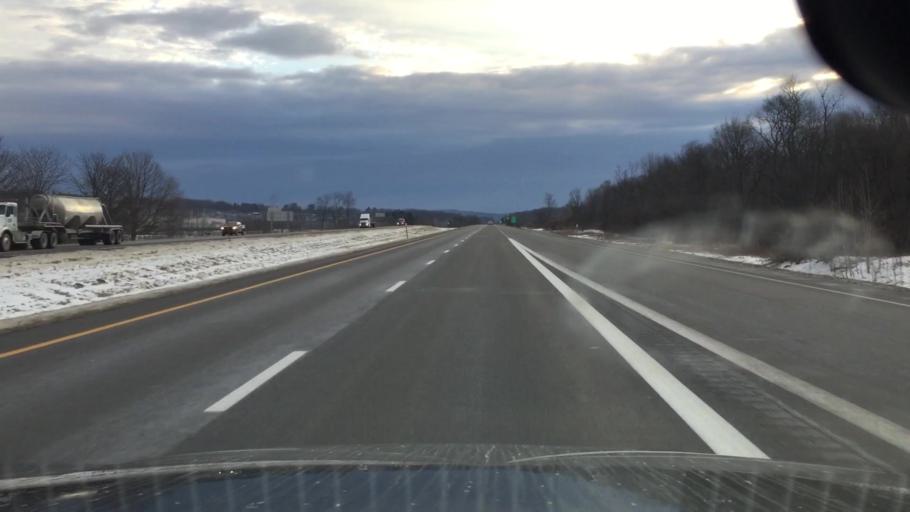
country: US
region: Pennsylvania
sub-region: Bradford County
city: South Waverly
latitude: 42.0007
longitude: -76.5837
